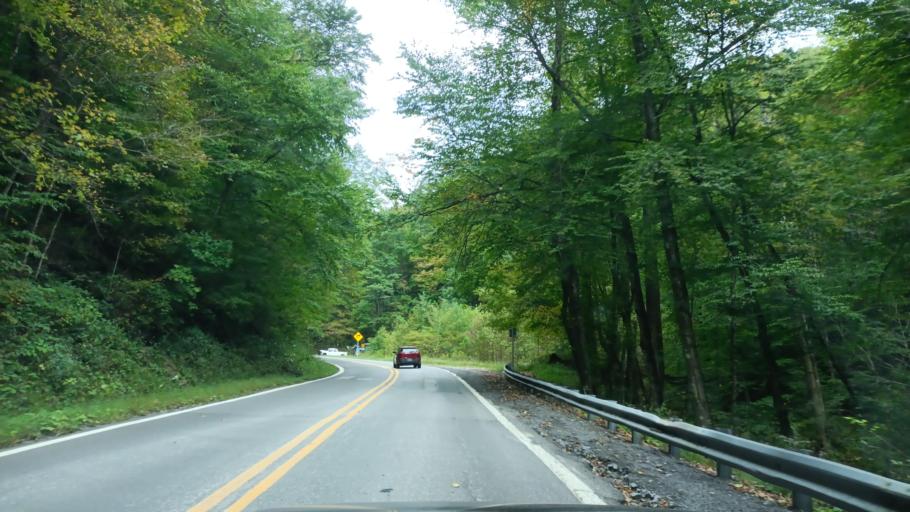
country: US
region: West Virginia
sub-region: Preston County
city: Kingwood
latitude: 39.3290
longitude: -79.7257
